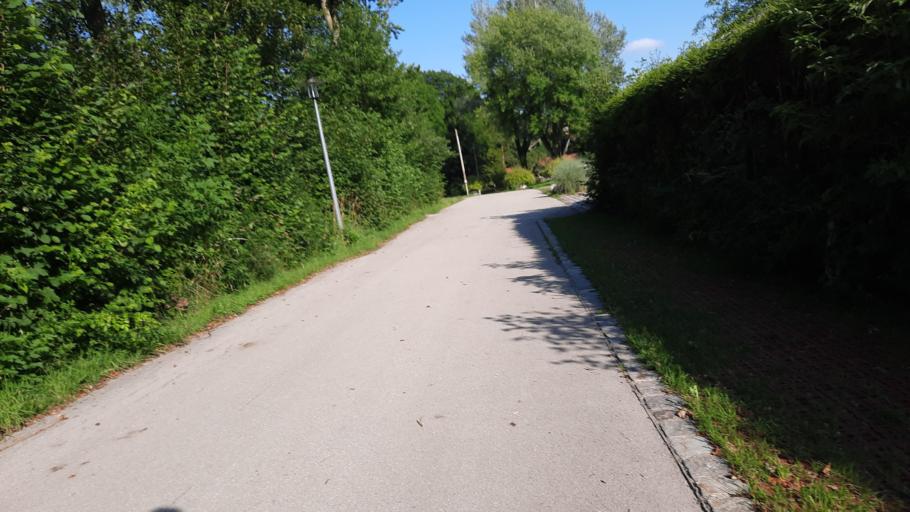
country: DE
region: Bavaria
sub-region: Upper Bavaria
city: Glonn
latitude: 47.9579
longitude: 11.8957
